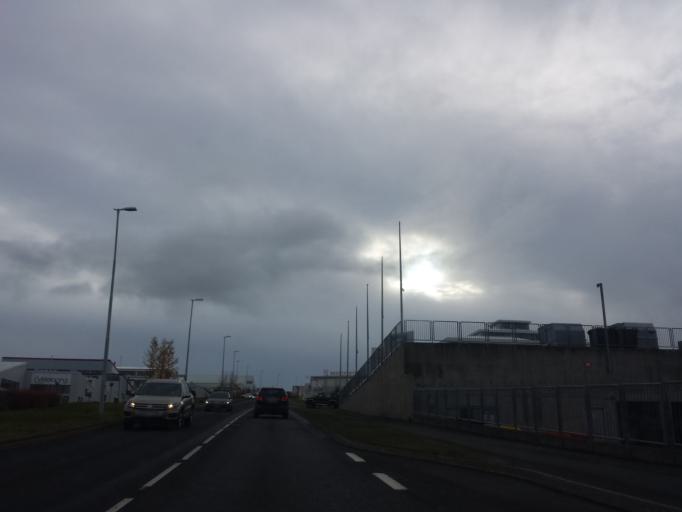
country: IS
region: Capital Region
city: Reykjavik
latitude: 64.1233
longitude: -21.7970
